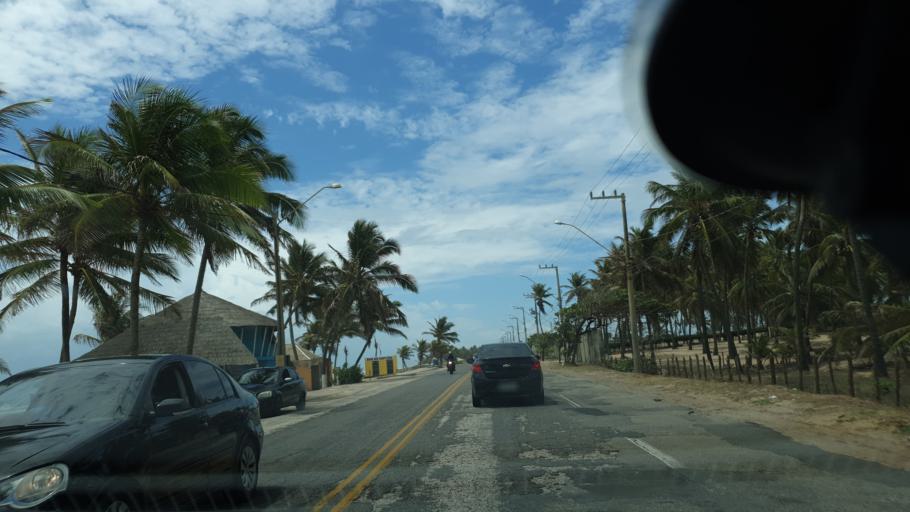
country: BR
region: Sergipe
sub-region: Sao Cristovao
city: Sao Cristovao
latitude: -11.0464
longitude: -37.0892
